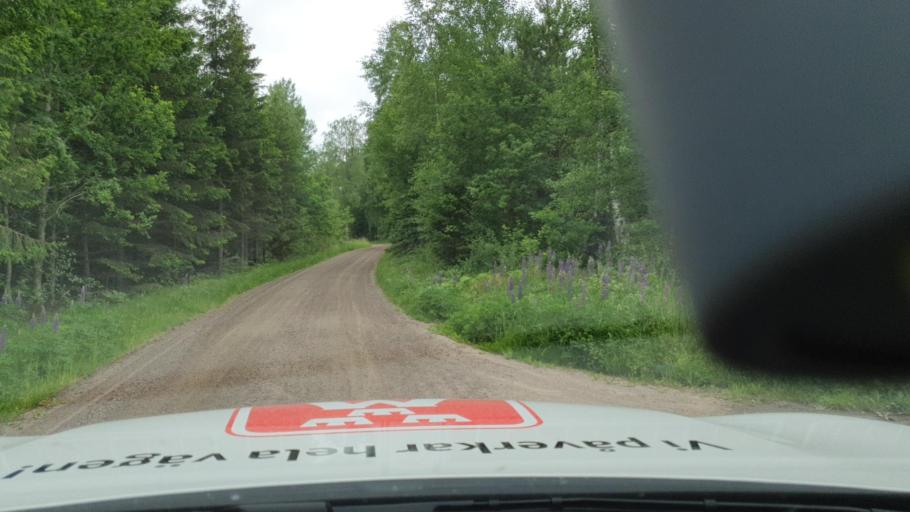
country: SE
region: Vaestra Goetaland
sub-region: Hjo Kommun
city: Hjo
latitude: 58.3473
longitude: 14.2997
